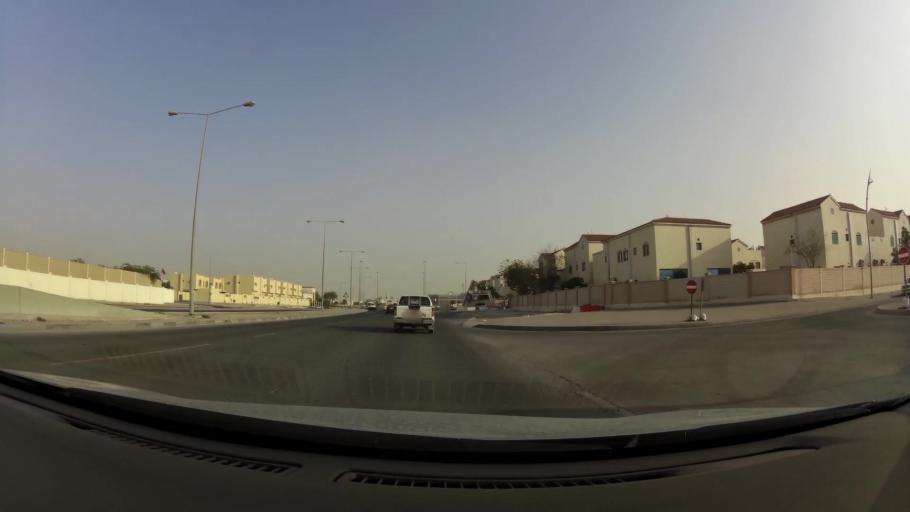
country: QA
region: Baladiyat ar Rayyan
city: Ar Rayyan
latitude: 25.2466
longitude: 51.4616
